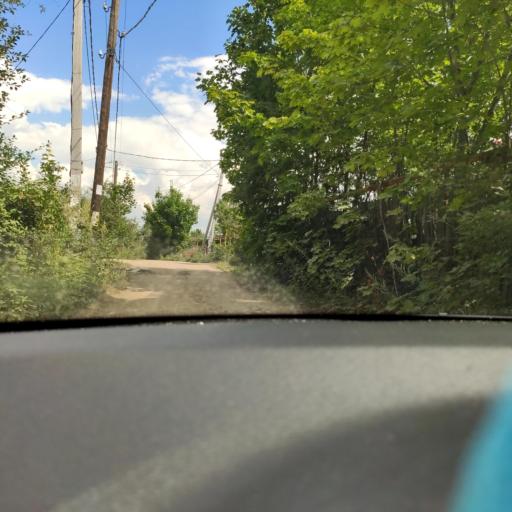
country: RU
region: Samara
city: Samara
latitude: 53.2963
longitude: 50.2300
